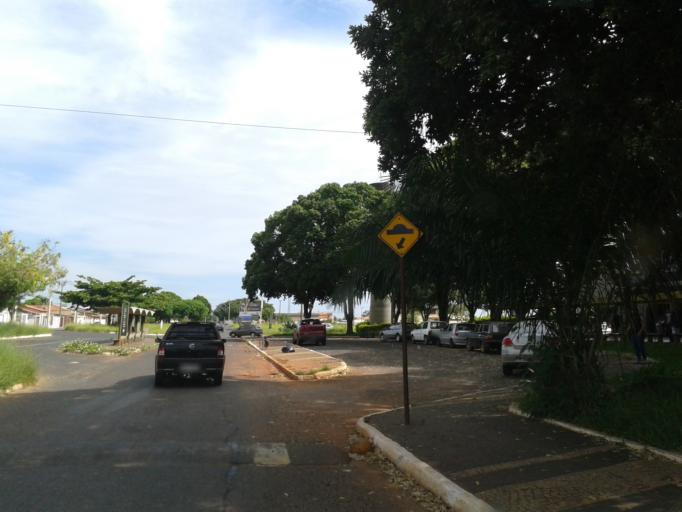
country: BR
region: Minas Gerais
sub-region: Araguari
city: Araguari
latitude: -18.6399
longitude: -48.1754
